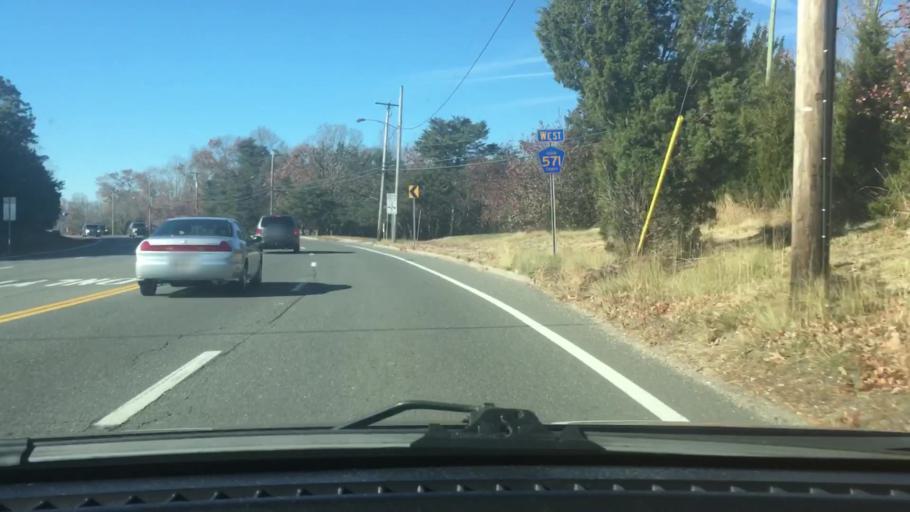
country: US
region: New Jersey
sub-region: Ocean County
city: Silver Ridge
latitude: 39.9914
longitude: -74.2039
